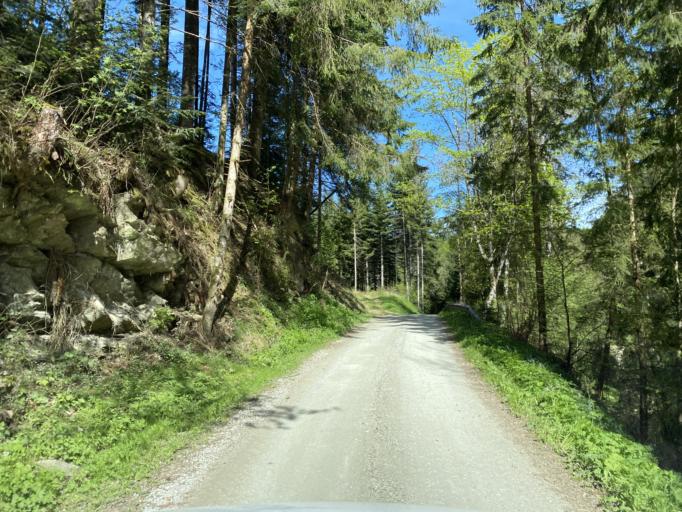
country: AT
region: Styria
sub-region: Politischer Bezirk Weiz
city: Gschaid bei Birkfeld
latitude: 47.3420
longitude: 15.7095
